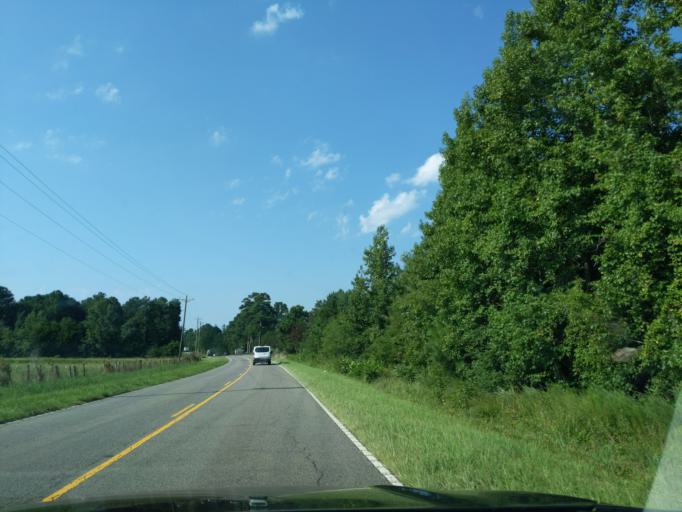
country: US
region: South Carolina
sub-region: Lexington County
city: Leesville
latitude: 33.9813
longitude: -81.5260
